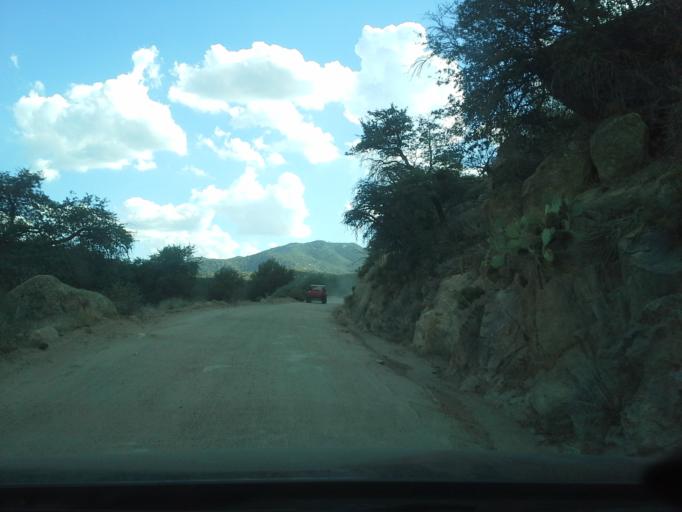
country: US
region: Arizona
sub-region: Yavapai County
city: Mayer
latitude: 34.2303
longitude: -112.3098
